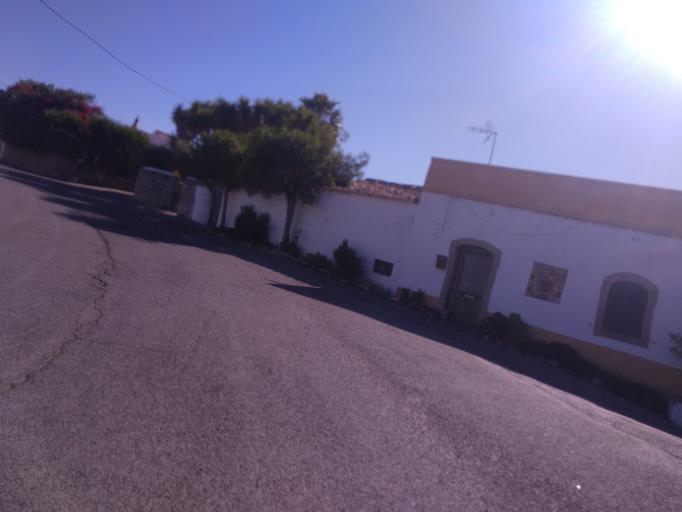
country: PT
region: Faro
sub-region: Sao Bras de Alportel
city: Sao Bras de Alportel
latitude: 37.1707
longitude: -7.8892
